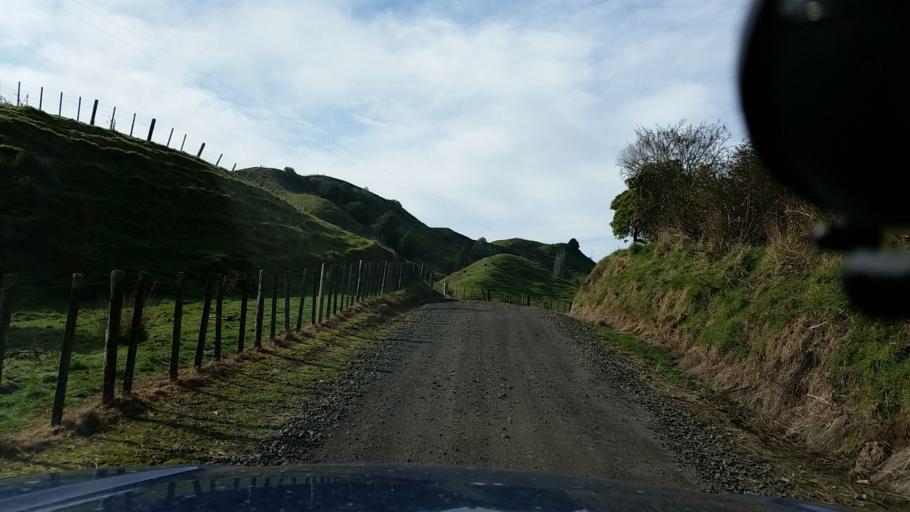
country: NZ
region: Taranaki
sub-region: New Plymouth District
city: Waitara
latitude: -39.0329
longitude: 174.7769
